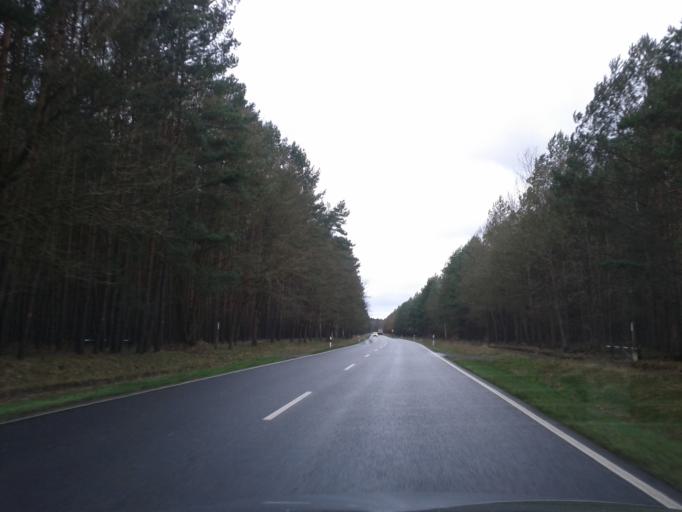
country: DE
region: Brandenburg
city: Rauen
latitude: 52.3772
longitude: 13.9923
